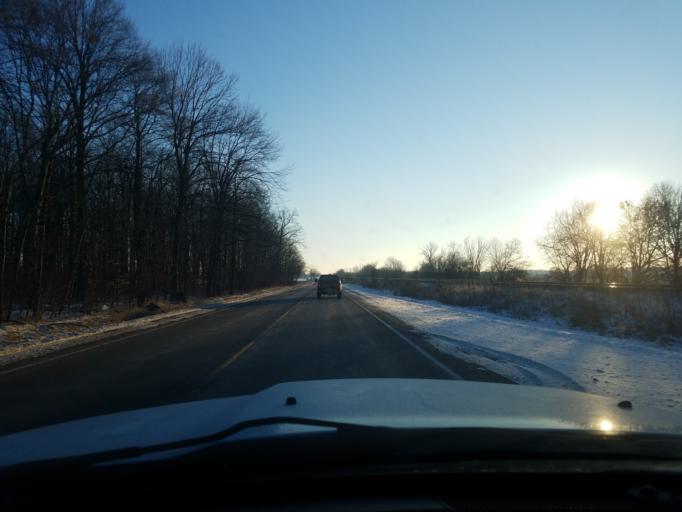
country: US
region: Indiana
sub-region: Elkhart County
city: Nappanee
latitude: 41.4454
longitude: -86.0585
